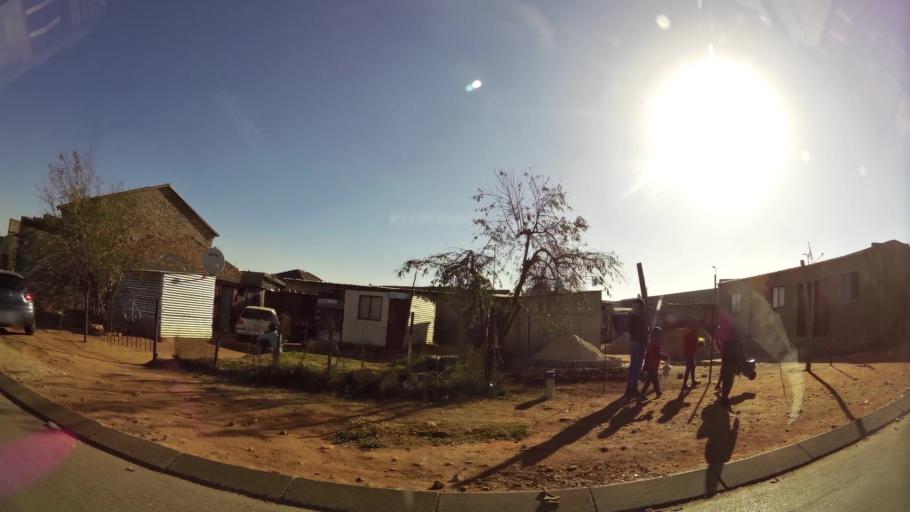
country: ZA
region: Gauteng
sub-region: Ekurhuleni Metropolitan Municipality
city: Tembisa
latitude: -26.0299
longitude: 28.2151
